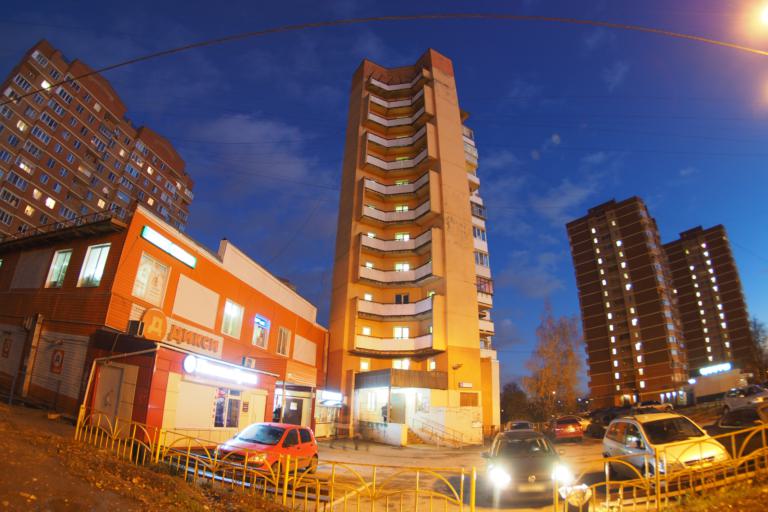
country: RU
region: Moskovskaya
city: Lobnya
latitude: 56.0195
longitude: 37.4226
